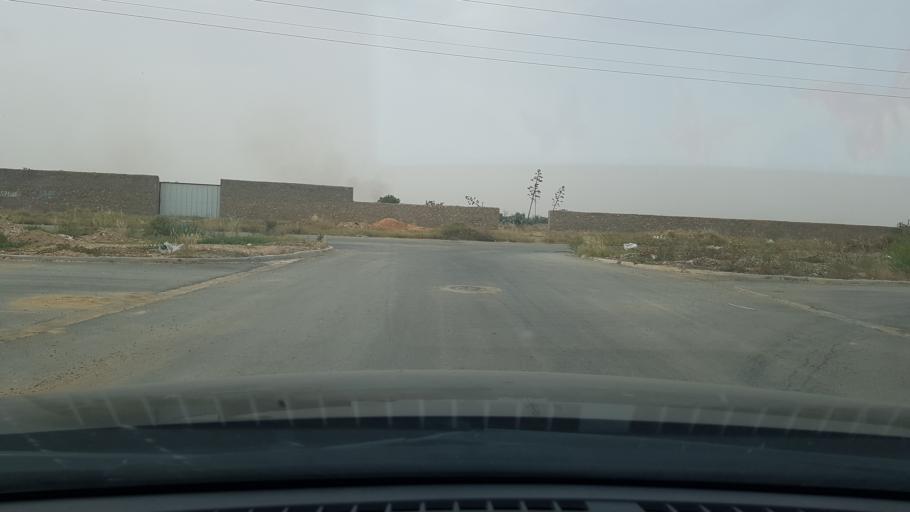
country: TN
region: Safaqis
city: Al Qarmadah
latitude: 34.8291
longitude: 10.7412
